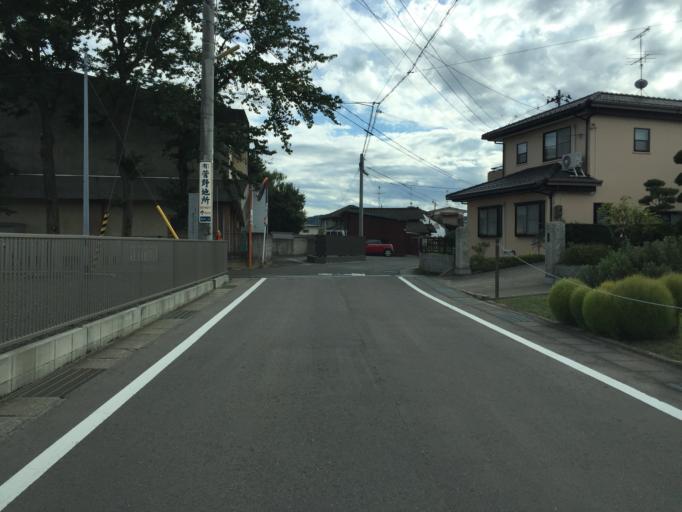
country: JP
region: Fukushima
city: Fukushima-shi
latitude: 37.8054
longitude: 140.4897
